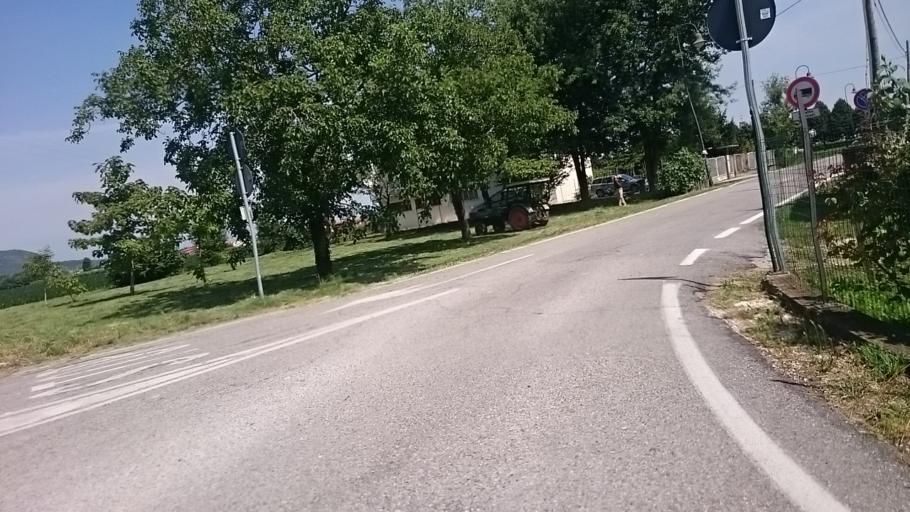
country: IT
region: Veneto
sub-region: Provincia di Vicenza
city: Villaganzerla
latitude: 45.4469
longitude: 11.6380
